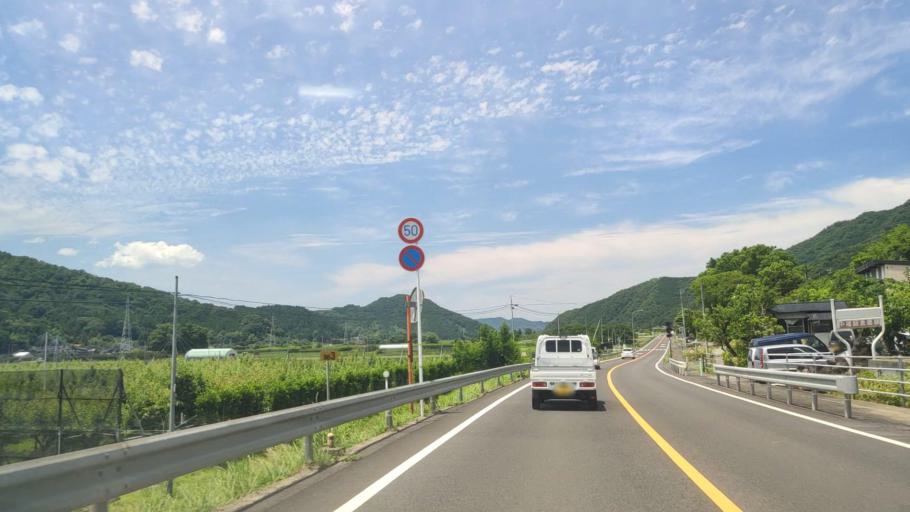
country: JP
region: Tottori
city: Tottori
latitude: 35.3676
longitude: 134.3132
